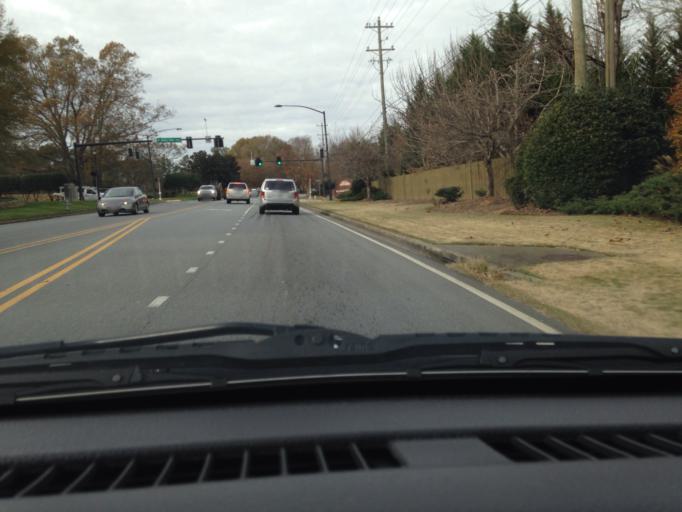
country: US
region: Georgia
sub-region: Fulton County
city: Johns Creek
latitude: 34.0782
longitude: -84.1837
